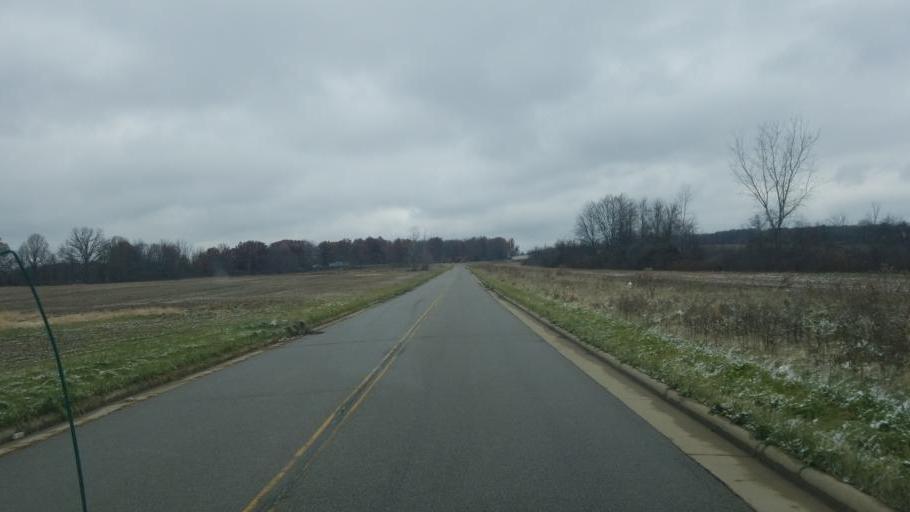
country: US
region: Ohio
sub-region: Richland County
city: Mansfield
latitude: 40.8085
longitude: -82.5379
